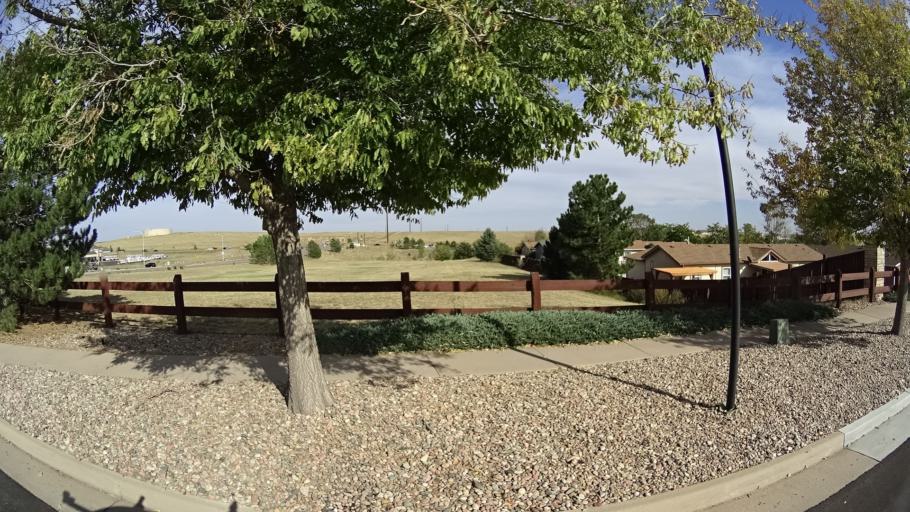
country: US
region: Colorado
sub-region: El Paso County
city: Cimarron Hills
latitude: 38.9001
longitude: -104.6864
